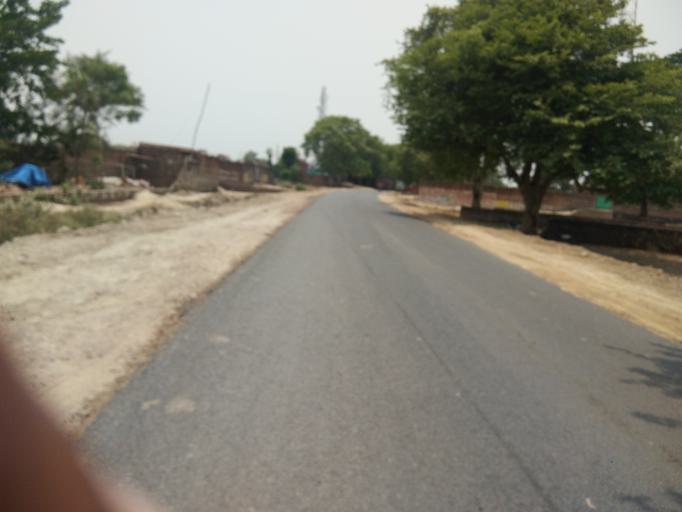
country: IN
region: Uttar Pradesh
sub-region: Ghazipur
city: Zamania
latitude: 25.4340
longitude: 83.6764
